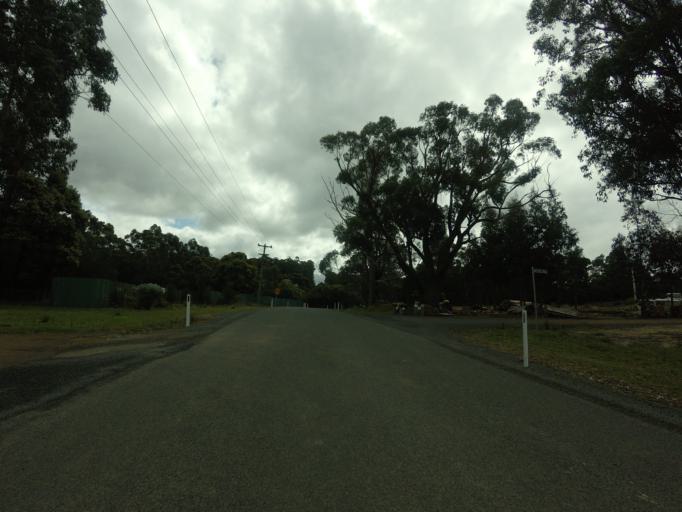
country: AU
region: Tasmania
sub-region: Huon Valley
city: Geeveston
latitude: -43.4311
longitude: 146.9036
